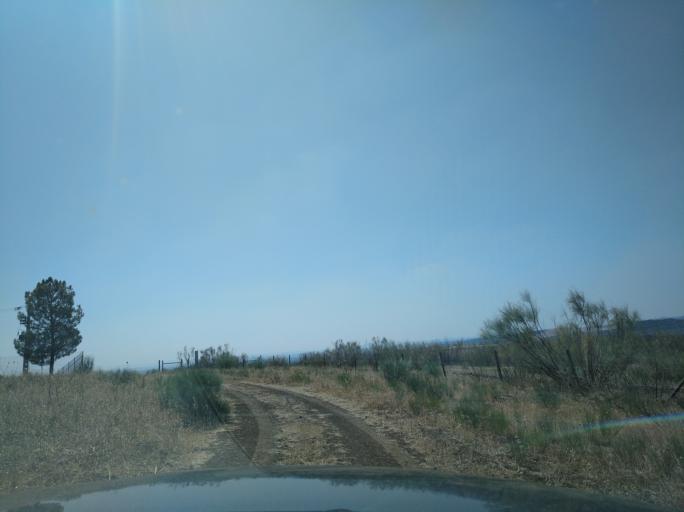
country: PT
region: Portalegre
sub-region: Campo Maior
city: Campo Maior
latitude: 39.0042
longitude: -7.0922
